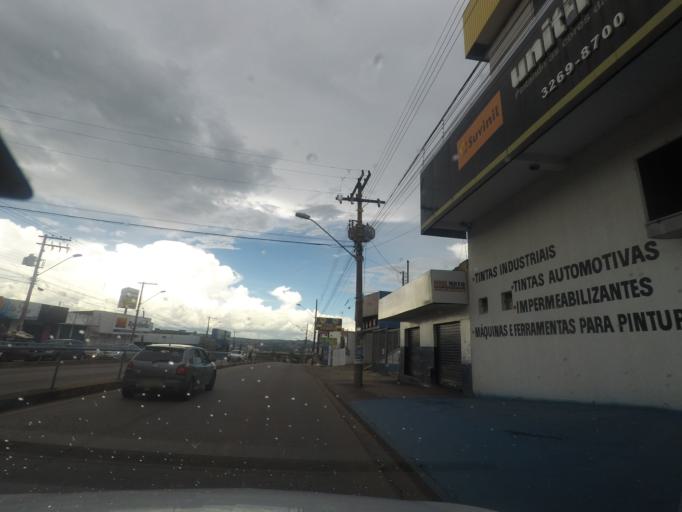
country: BR
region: Goias
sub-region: Goiania
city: Goiania
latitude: -16.6707
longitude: -49.2299
